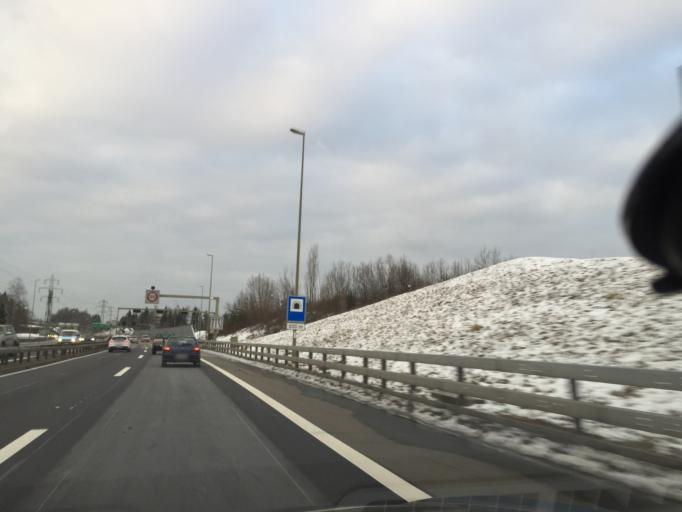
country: CH
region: Zurich
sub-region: Bezirk Horgen
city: Kilchberg / Baechler-Stocken
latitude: 47.3279
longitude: 8.5306
